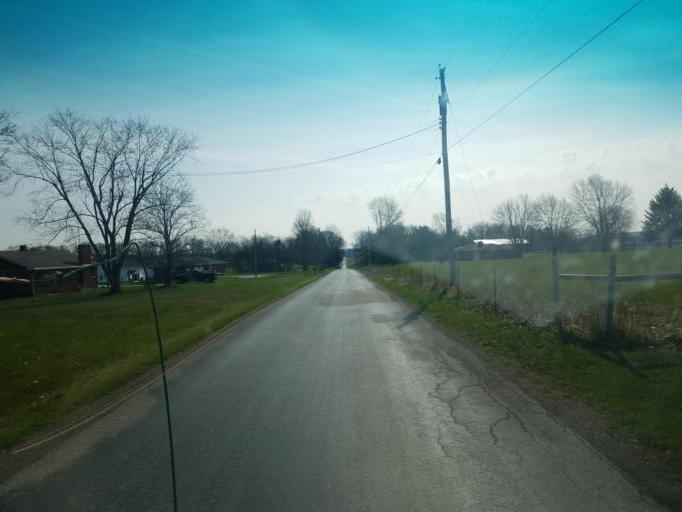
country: US
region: Ohio
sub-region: Richland County
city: Lincoln Heights
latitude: 40.8730
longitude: -82.5088
